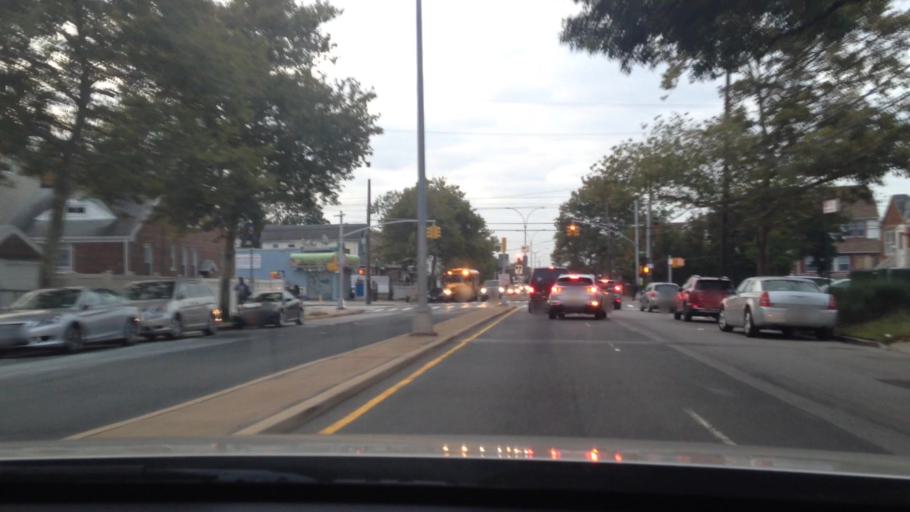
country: US
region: New York
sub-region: Nassau County
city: Bellerose Terrace
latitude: 40.7109
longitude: -73.7527
